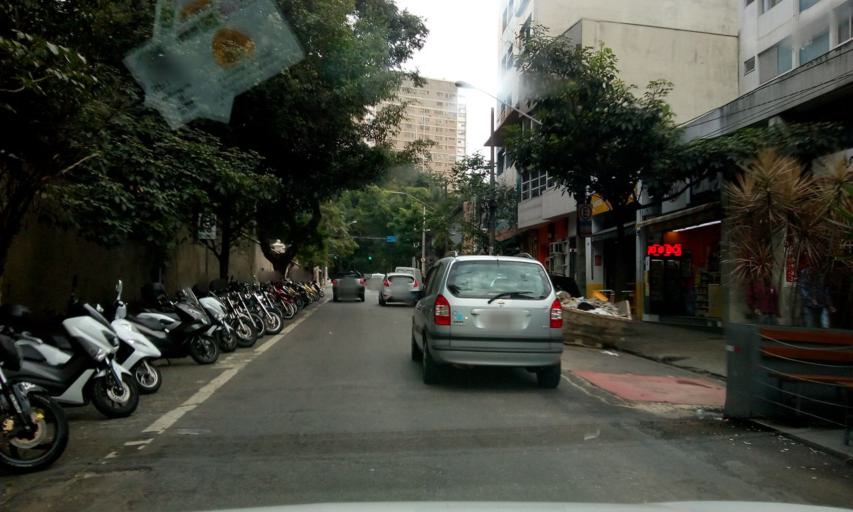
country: BR
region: Sao Paulo
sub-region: Sao Paulo
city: Sao Paulo
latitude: -23.5460
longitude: -46.6512
